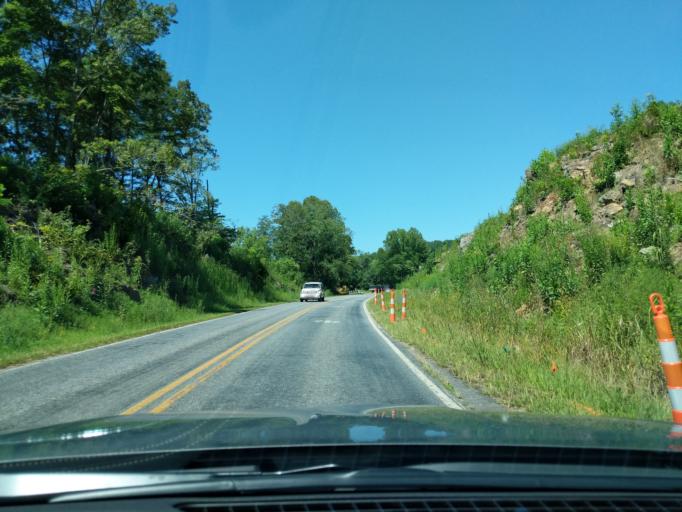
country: US
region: Georgia
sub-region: Towns County
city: Hiawassee
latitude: 35.0249
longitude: -83.7318
